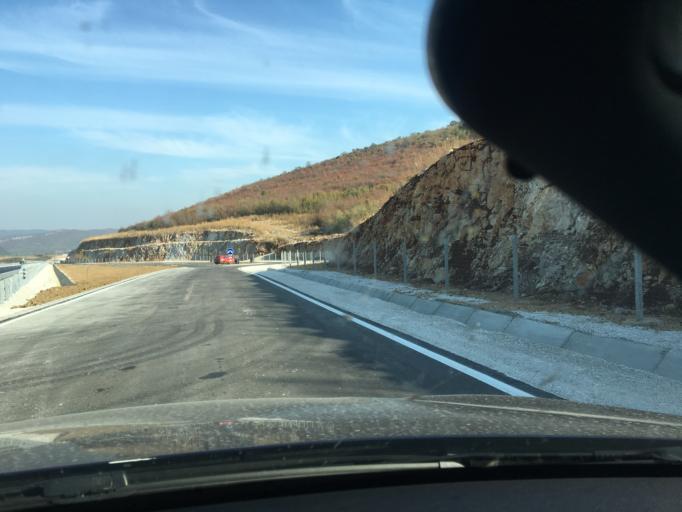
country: BG
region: Lovech
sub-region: Obshtina Yablanitsa
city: Yablanitsa
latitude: 43.0531
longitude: 24.1940
